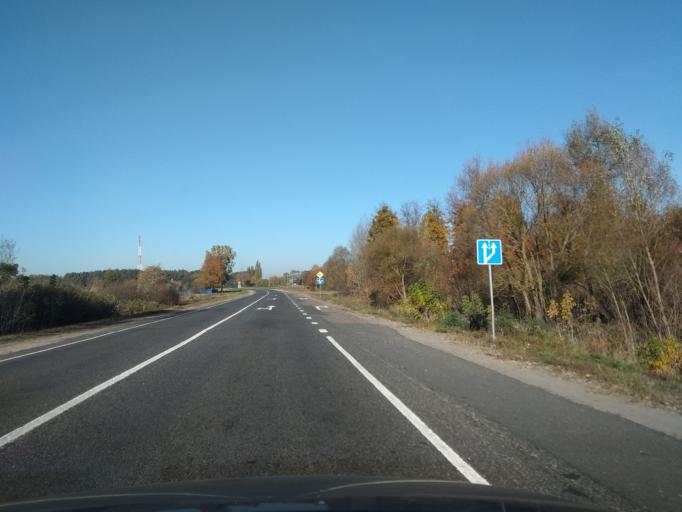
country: BY
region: Brest
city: Malaryta
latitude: 51.9260
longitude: 24.0720
